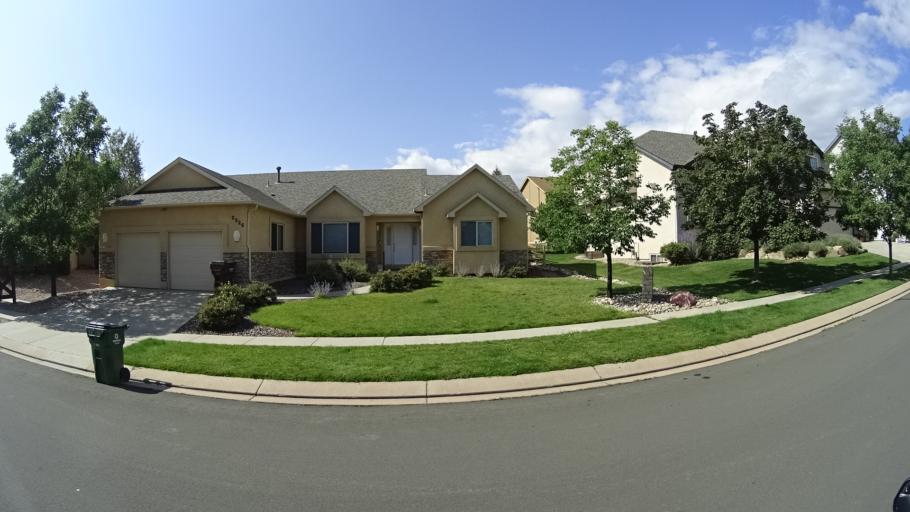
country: US
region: Colorado
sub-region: El Paso County
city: Manitou Springs
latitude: 38.9148
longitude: -104.8704
